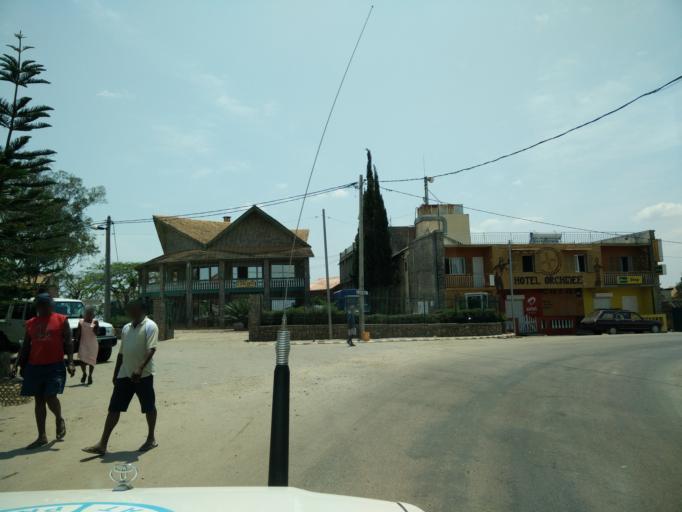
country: MG
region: Ihorombe
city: Ranohira
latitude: -22.5570
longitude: 45.4141
